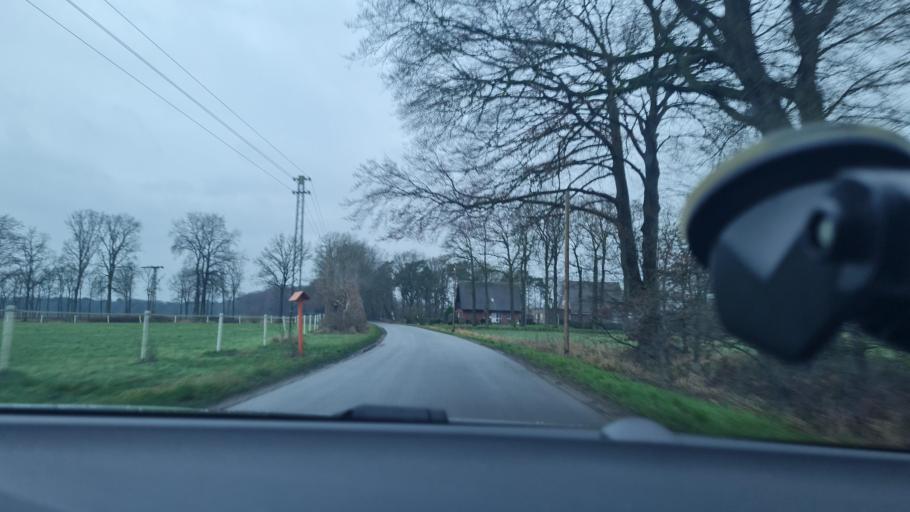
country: DE
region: North Rhine-Westphalia
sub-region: Regierungsbezirk Munster
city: Raesfeld
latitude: 51.7689
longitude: 6.9058
